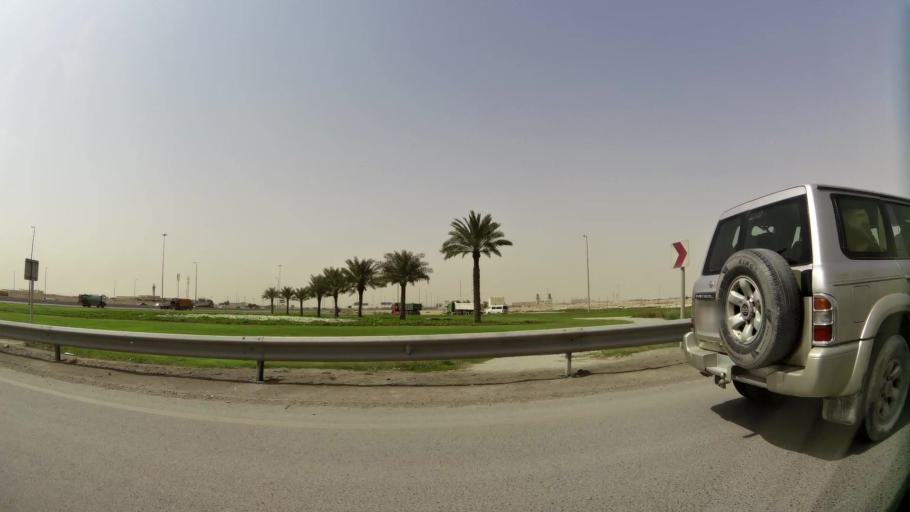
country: QA
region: Baladiyat ar Rayyan
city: Ar Rayyan
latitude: 25.2110
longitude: 51.4043
